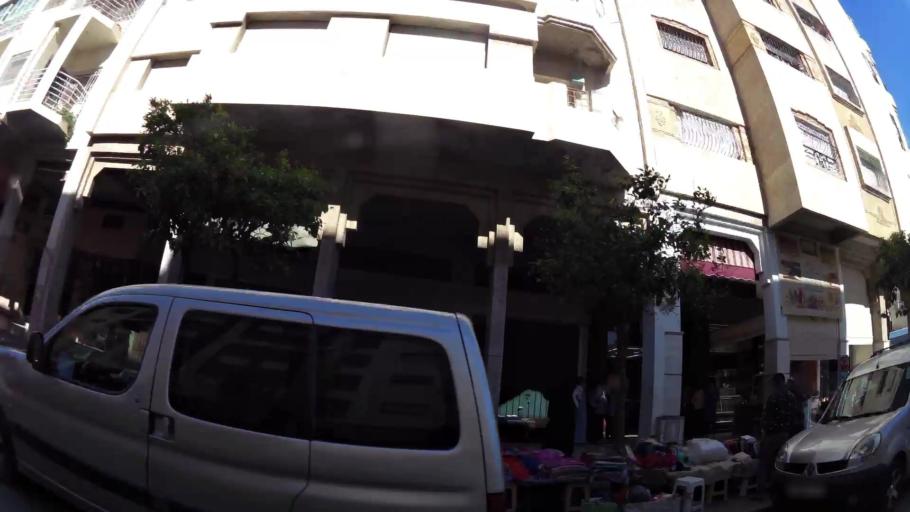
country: MA
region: Fes-Boulemane
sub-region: Fes
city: Fes
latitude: 34.0175
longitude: -4.9815
